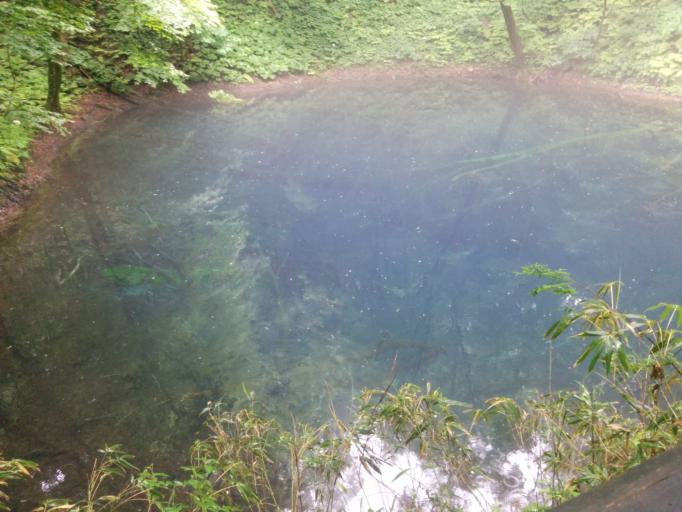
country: JP
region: Akita
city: Noshiromachi
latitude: 40.5607
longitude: 139.9851
